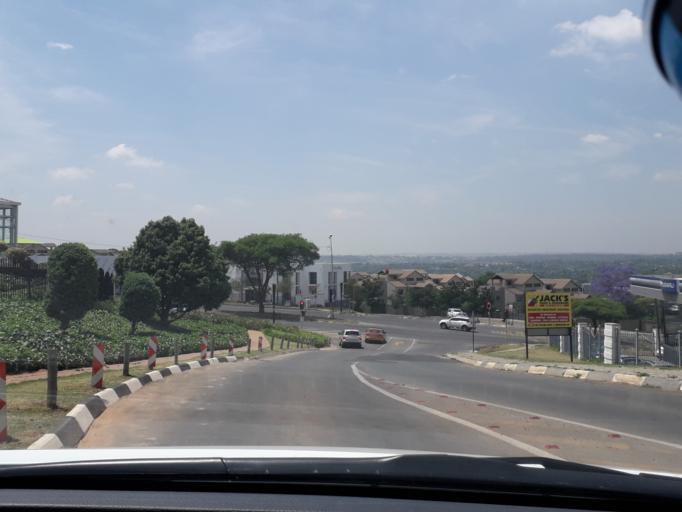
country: ZA
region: Gauteng
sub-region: City of Johannesburg Metropolitan Municipality
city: Midrand
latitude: -26.0674
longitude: 28.0244
